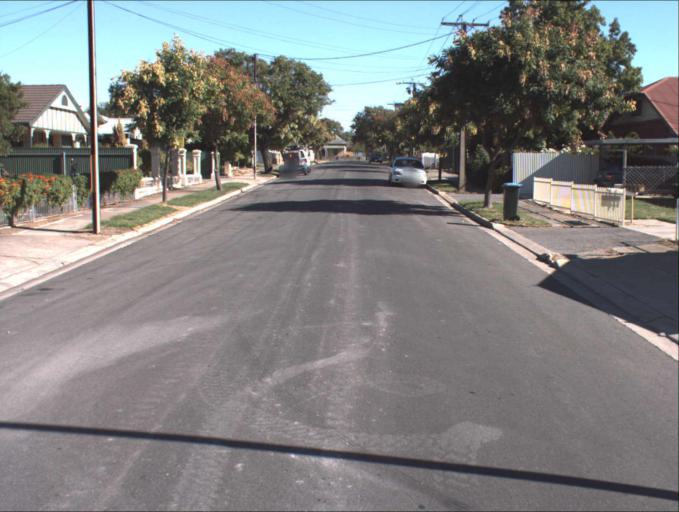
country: AU
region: South Australia
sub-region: Prospect
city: Prospect
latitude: -34.8739
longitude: 138.6049
